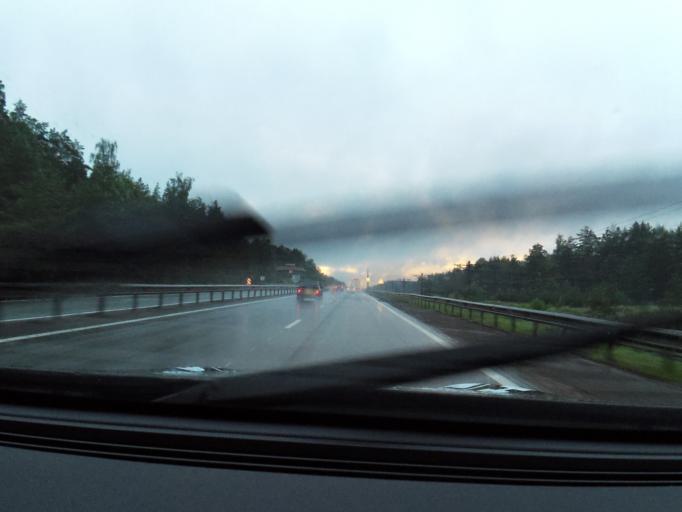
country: RU
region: Tatarstan
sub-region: Tukayevskiy Rayon
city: Naberezhnyye Chelny
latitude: 55.7260
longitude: 52.2576
